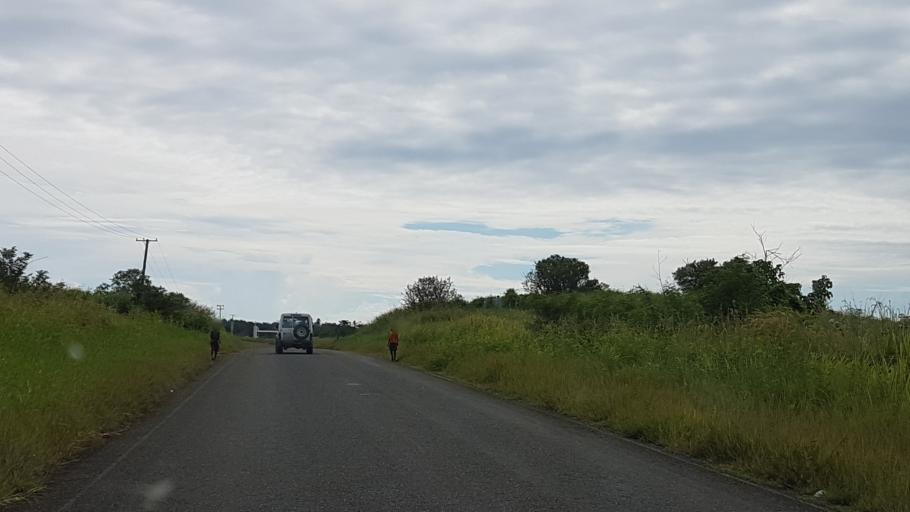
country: PG
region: Madang
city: Madang
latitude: -5.0594
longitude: 145.7928
